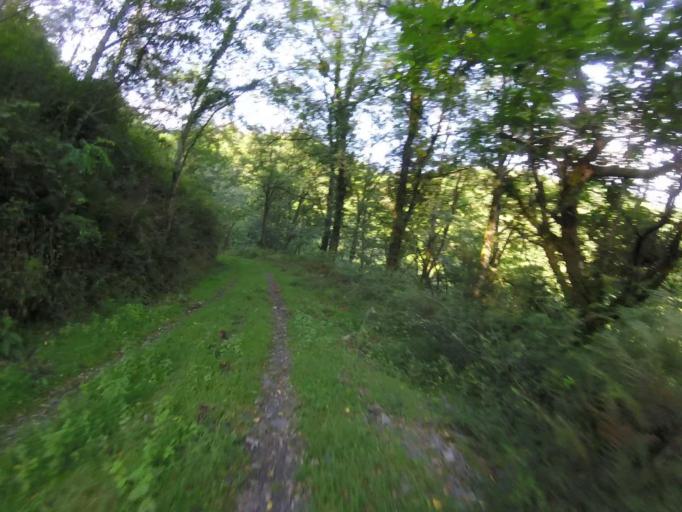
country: ES
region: Navarre
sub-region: Provincia de Navarra
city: Arano
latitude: 43.2281
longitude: -1.9123
